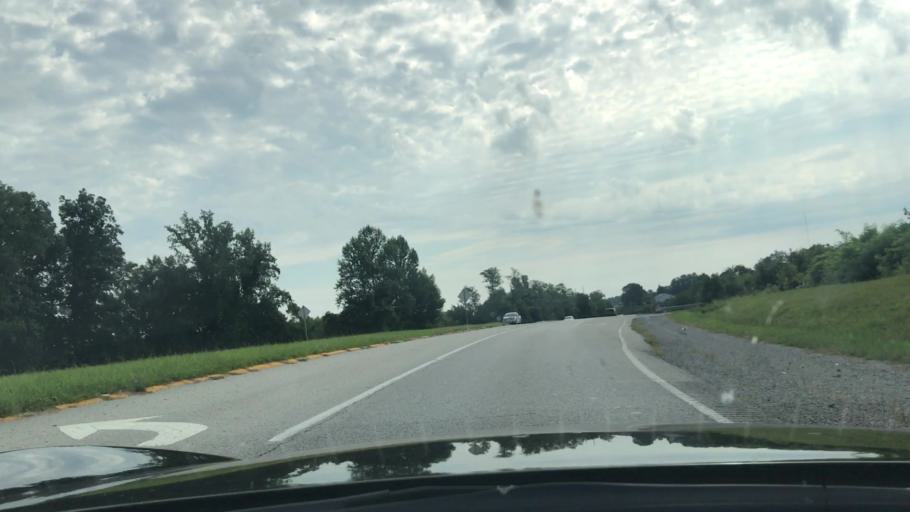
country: US
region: Kentucky
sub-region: Taylor County
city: Campbellsville
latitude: 37.3379
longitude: -85.3665
